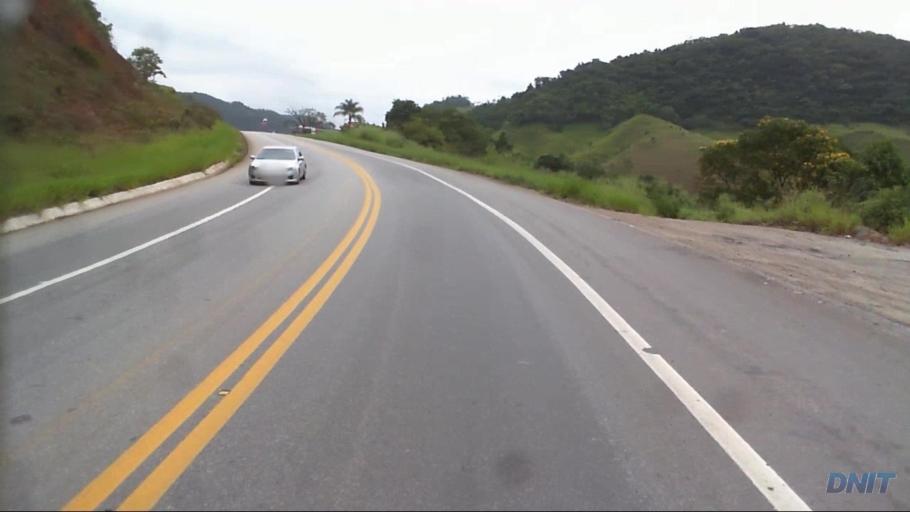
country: BR
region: Minas Gerais
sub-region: Timoteo
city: Timoteo
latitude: -19.6267
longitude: -42.8341
